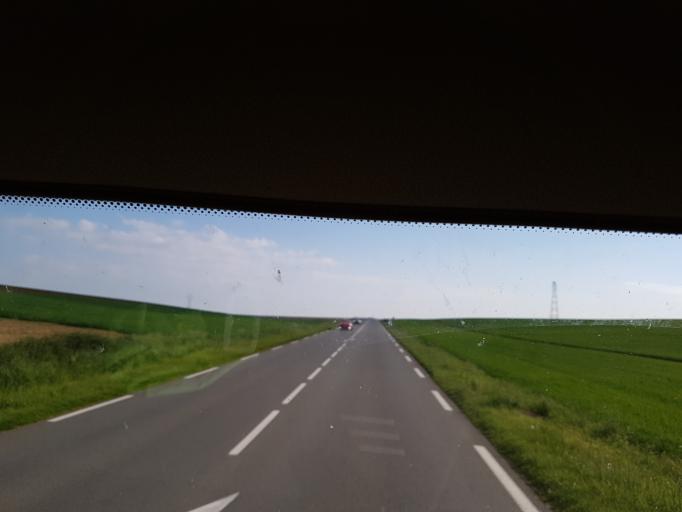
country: FR
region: Picardie
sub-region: Departement de la Somme
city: Crecy-en-Ponthieu
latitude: 50.2507
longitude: 1.9640
